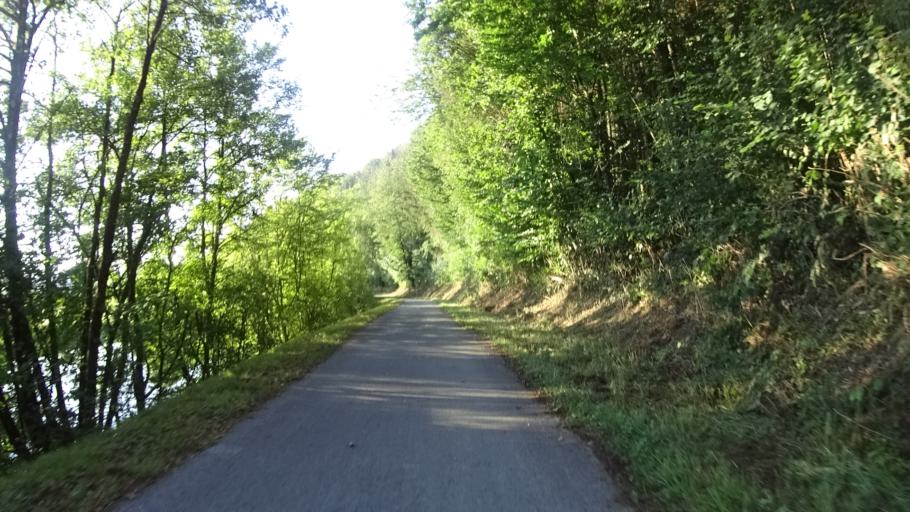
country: FR
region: Franche-Comte
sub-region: Territoire de Belfort
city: Mezire
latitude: 47.5415
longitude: 6.9073
